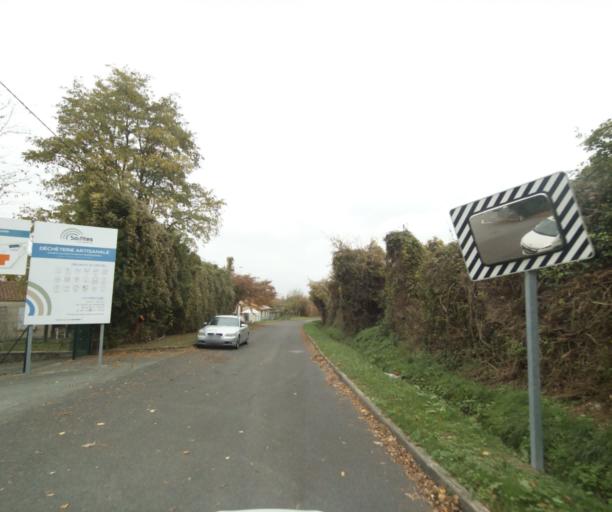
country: FR
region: Poitou-Charentes
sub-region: Departement de la Charente-Maritime
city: Saintes
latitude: 45.7217
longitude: -0.6437
